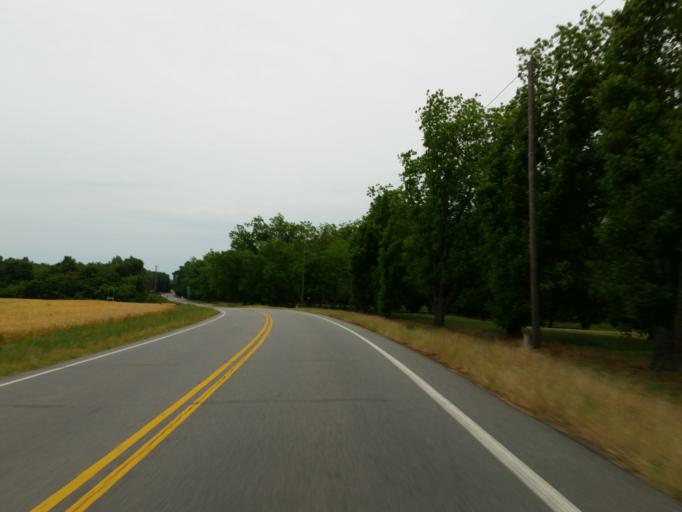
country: US
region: Georgia
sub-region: Dooly County
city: Unadilla
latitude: 32.2292
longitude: -83.7572
